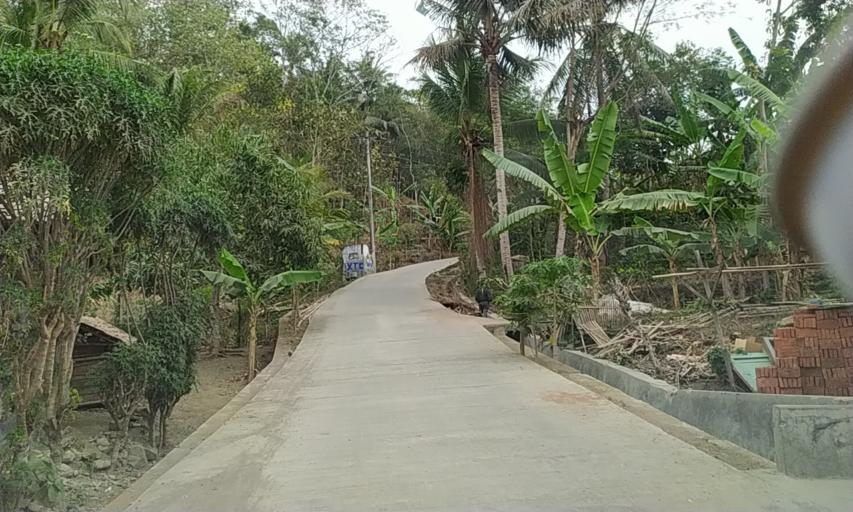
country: ID
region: Central Java
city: Genteng Wetan
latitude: -7.3586
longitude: 108.8932
